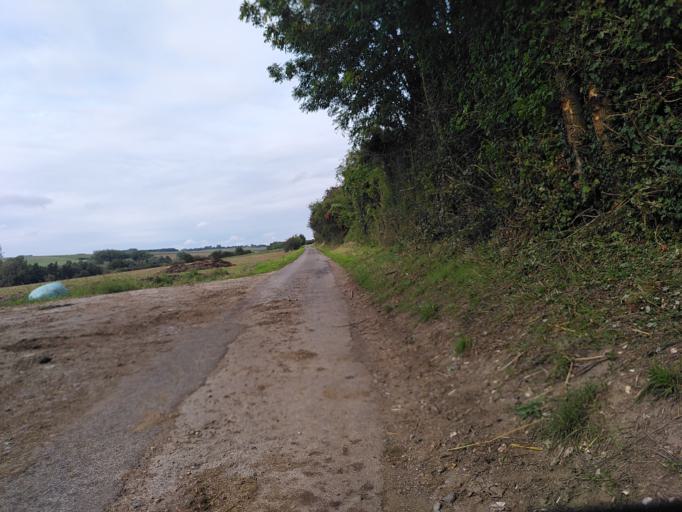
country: FR
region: Nord-Pas-de-Calais
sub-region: Departement du Pas-de-Calais
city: Therouanne
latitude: 50.6018
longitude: 2.1895
